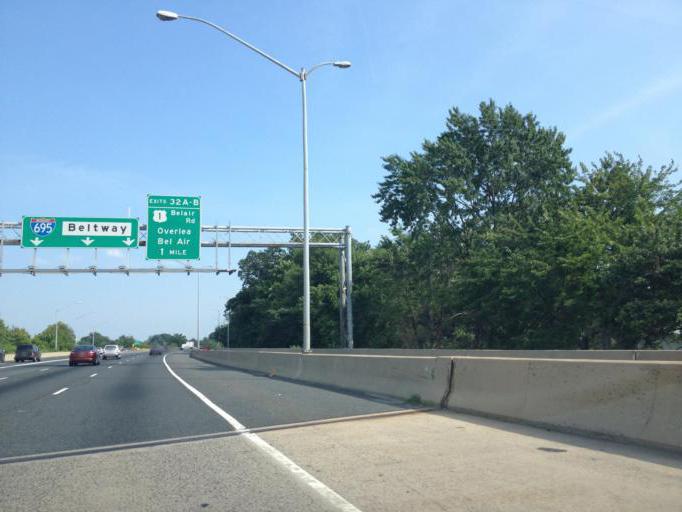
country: US
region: Maryland
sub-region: Baltimore County
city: Carney
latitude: 39.3847
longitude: -76.5239
